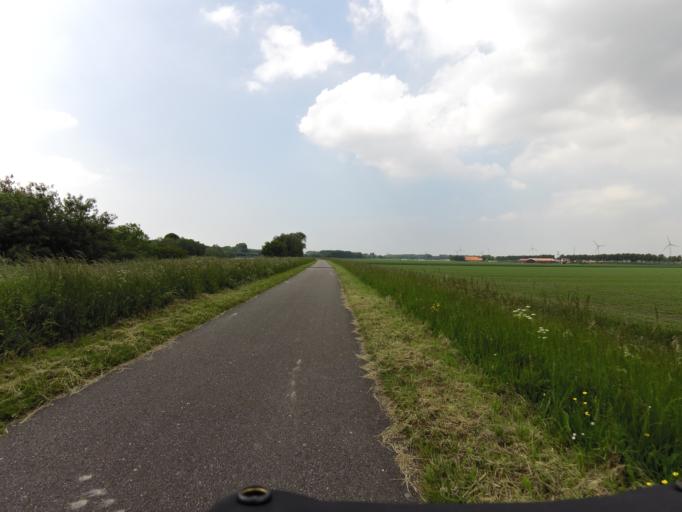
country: NL
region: South Holland
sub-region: Gemeente Spijkenisse
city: Spijkenisse
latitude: 51.8449
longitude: 4.2580
